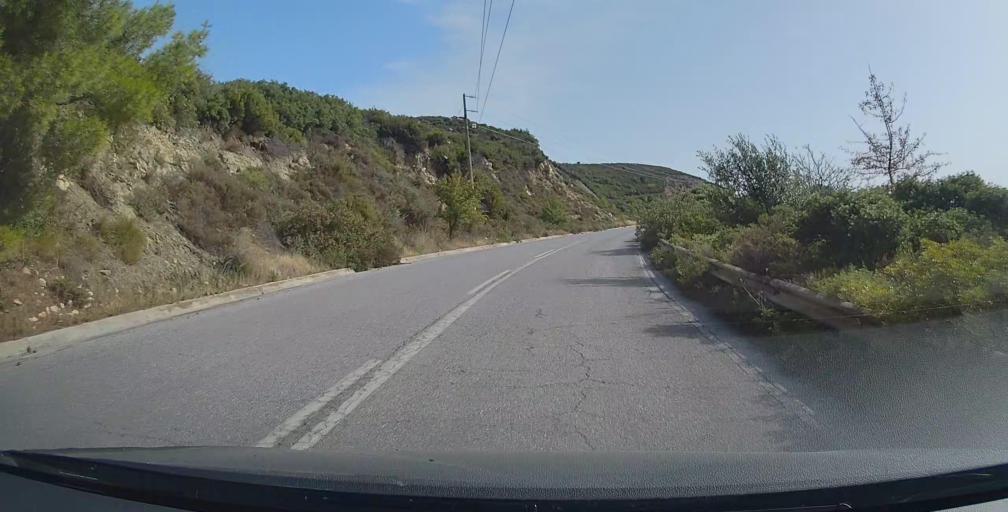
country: GR
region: Central Macedonia
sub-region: Nomos Chalkidikis
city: Sykia
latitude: 39.9675
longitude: 23.9517
